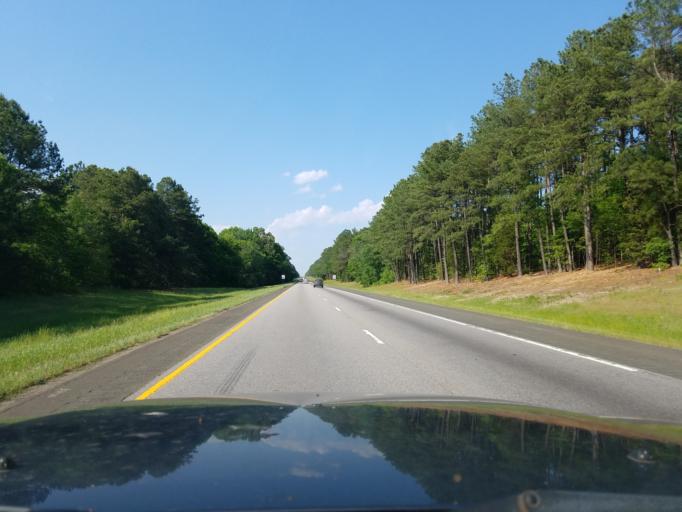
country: US
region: North Carolina
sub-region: Granville County
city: Butner
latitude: 36.0886
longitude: -78.7621
